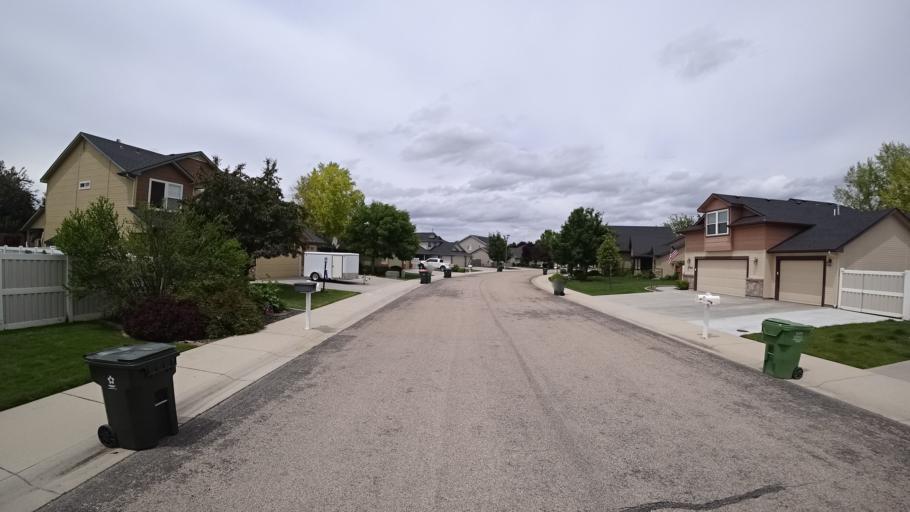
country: US
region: Idaho
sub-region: Ada County
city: Meridian
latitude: 43.6389
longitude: -116.3985
